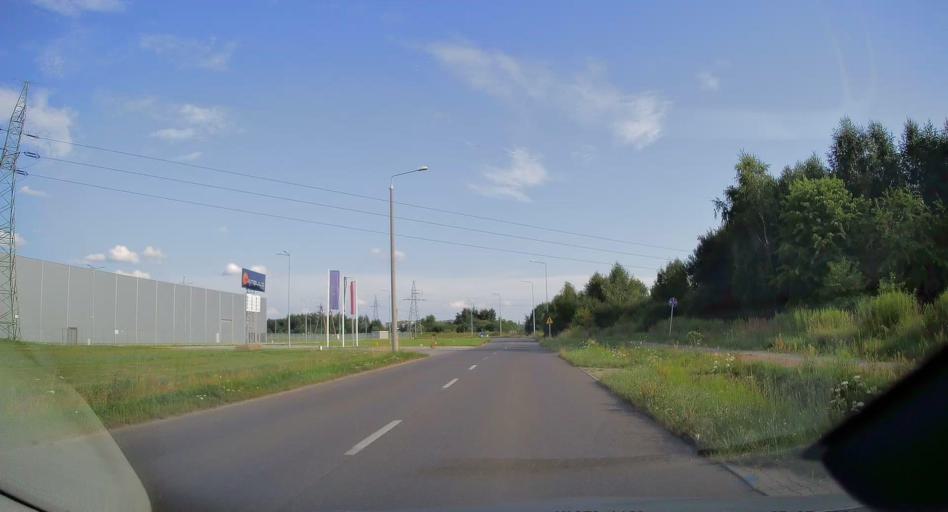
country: PL
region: Swietokrzyskie
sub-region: Powiat konecki
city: Konskie
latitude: 51.2090
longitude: 20.3964
